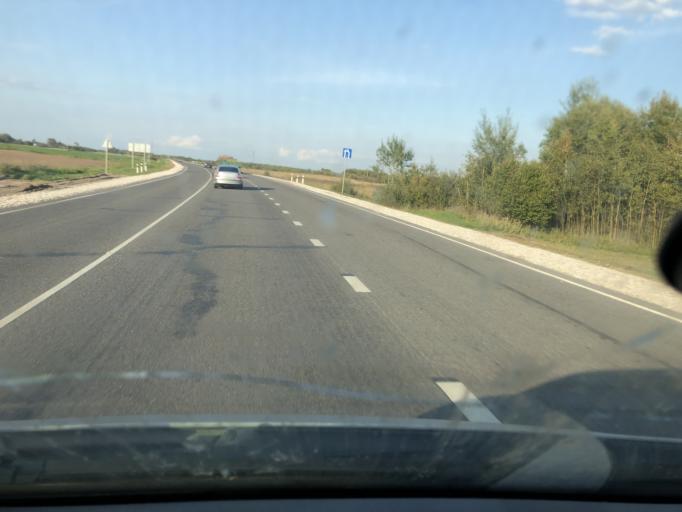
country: RU
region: Kaluga
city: Peremyshl'
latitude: 54.2555
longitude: 36.1247
